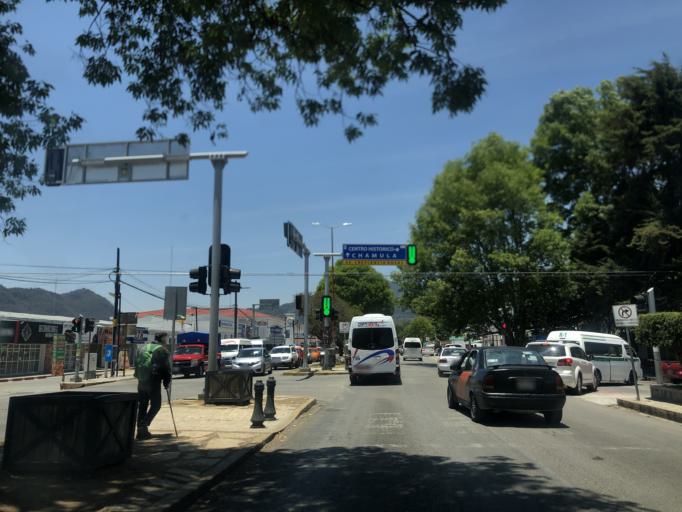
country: MX
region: Chiapas
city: San Cristobal de las Casas
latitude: 16.7303
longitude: -92.6386
